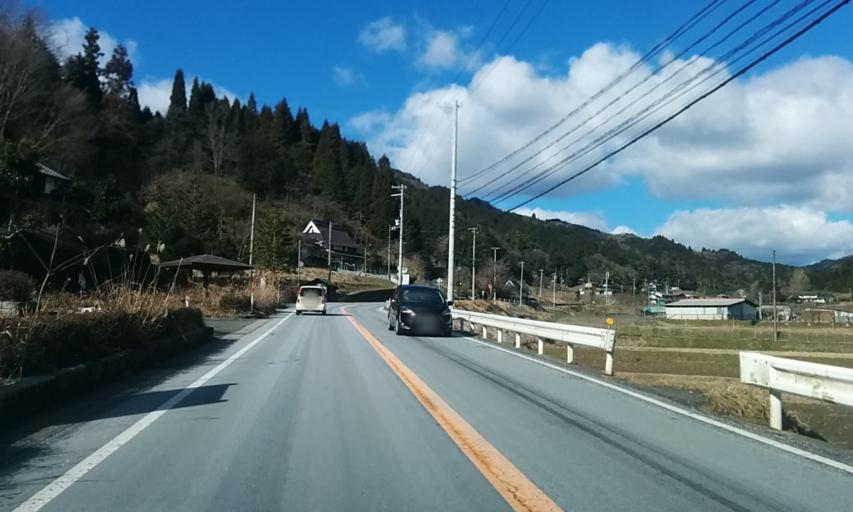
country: JP
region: Kyoto
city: Fukuchiyama
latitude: 35.3701
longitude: 135.0473
